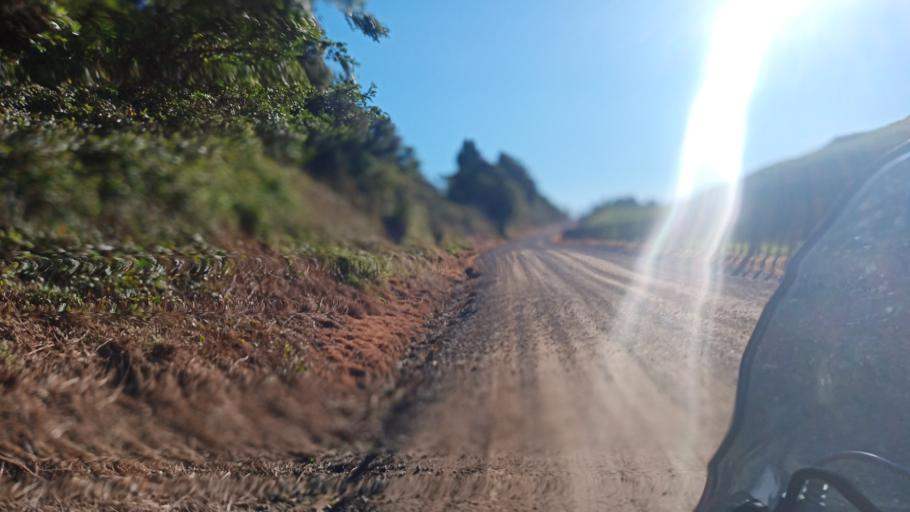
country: NZ
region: Hawke's Bay
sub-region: Wairoa District
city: Wairoa
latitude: -38.8057
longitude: 177.2890
